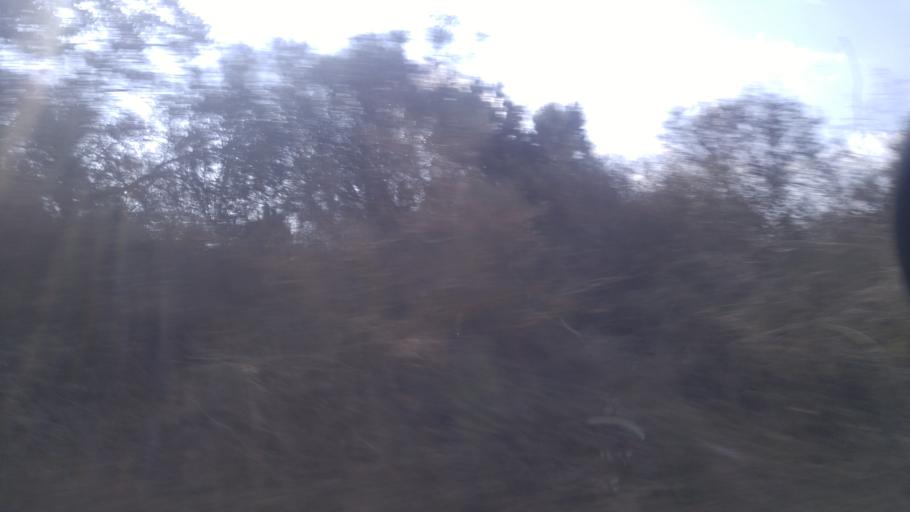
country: TR
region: Istanbul
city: Canta
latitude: 41.1699
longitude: 28.0955
